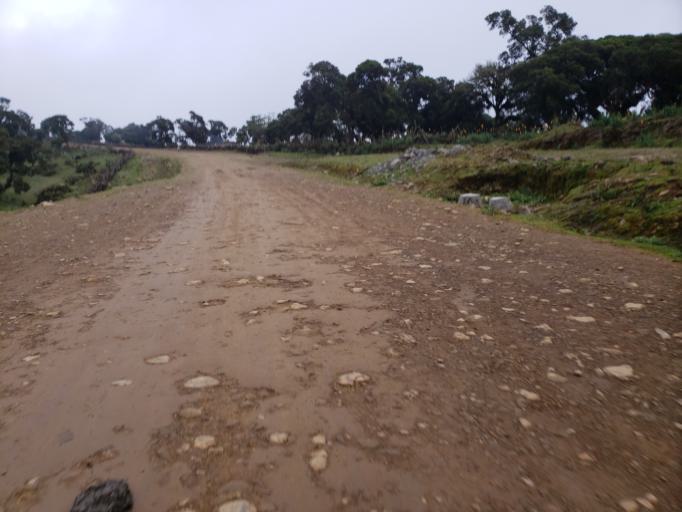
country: ET
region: Oromiya
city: Dodola
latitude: 6.7257
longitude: 39.4252
